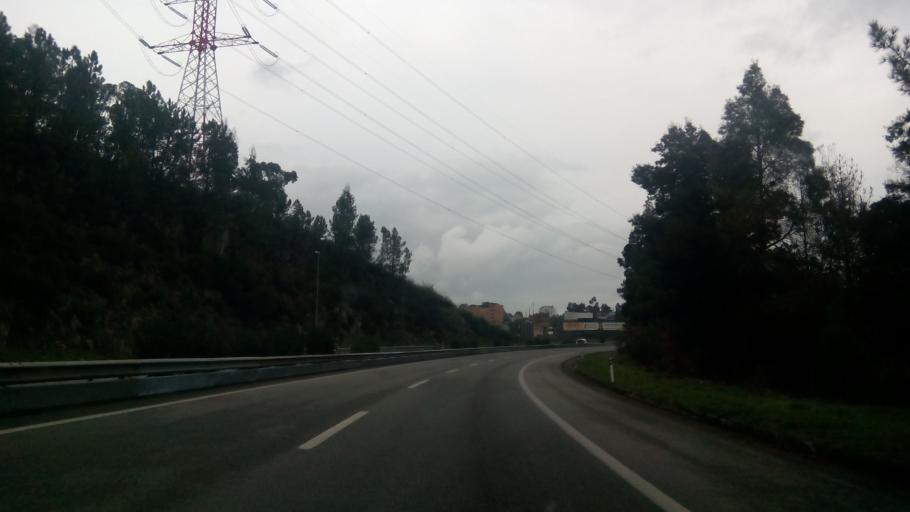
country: PT
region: Porto
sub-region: Paredes
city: Baltar
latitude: 41.1813
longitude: -8.3764
